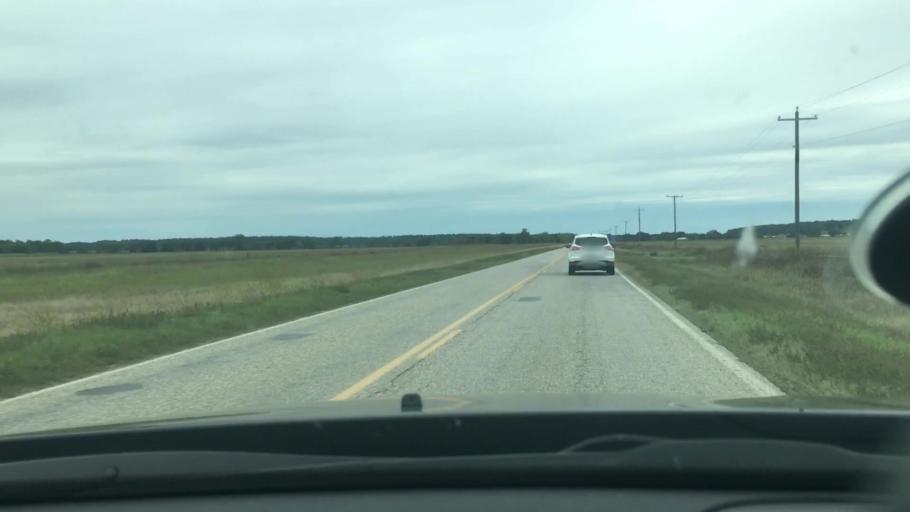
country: US
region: Oklahoma
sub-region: Johnston County
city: Tishomingo
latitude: 34.3393
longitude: -96.4211
